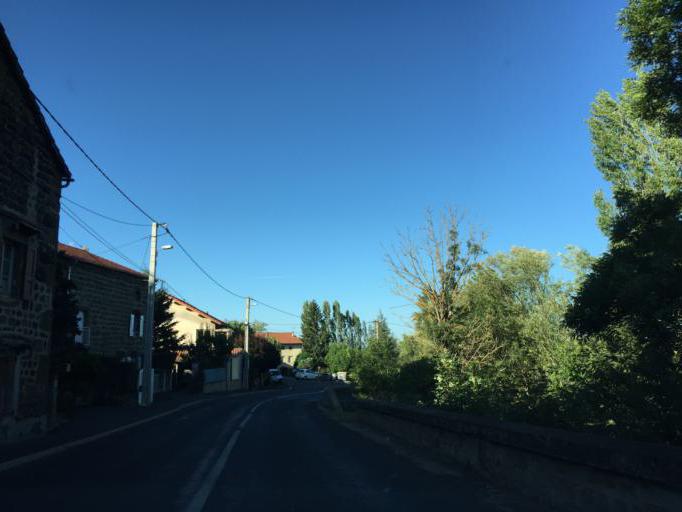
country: FR
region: Auvergne
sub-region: Departement de la Haute-Loire
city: Bains
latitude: 45.0097
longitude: 3.8009
